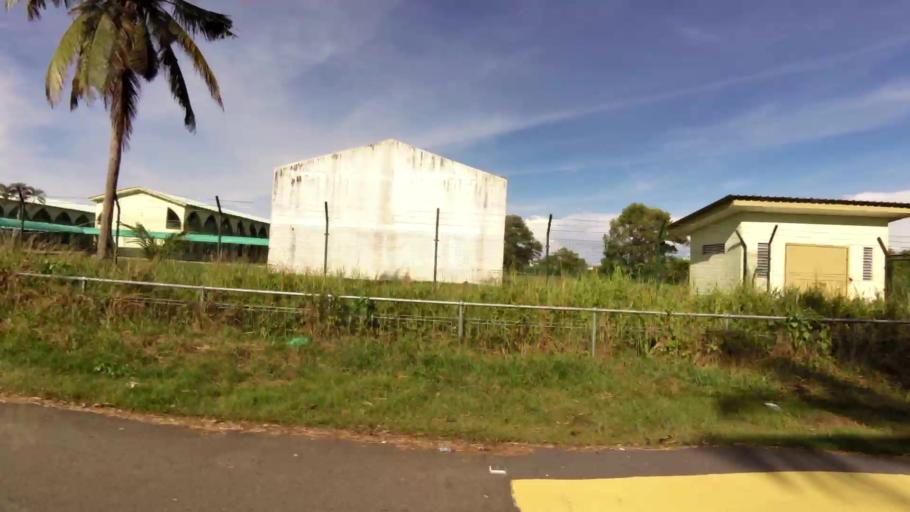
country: BN
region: Belait
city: Kuala Belait
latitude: 4.5759
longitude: 114.2040
